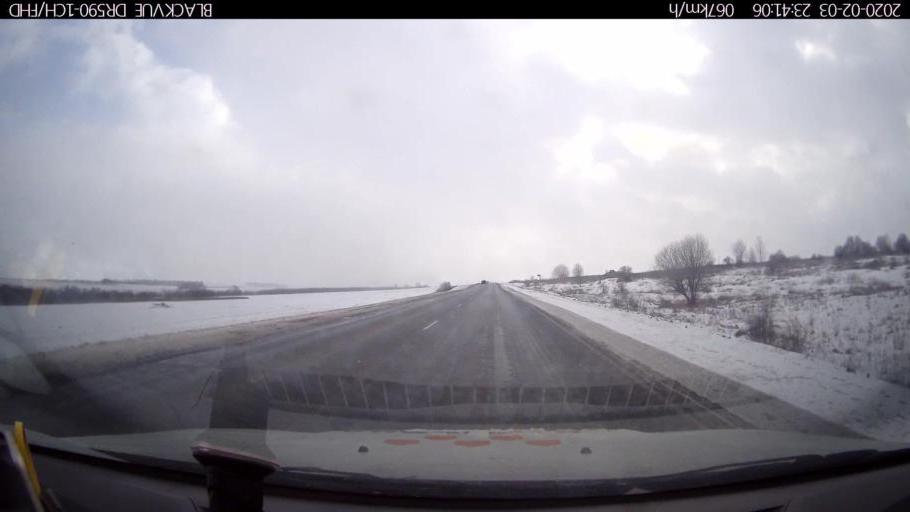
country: RU
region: Nizjnij Novgorod
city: Dal'neye Konstantinovo
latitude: 55.8663
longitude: 44.1328
